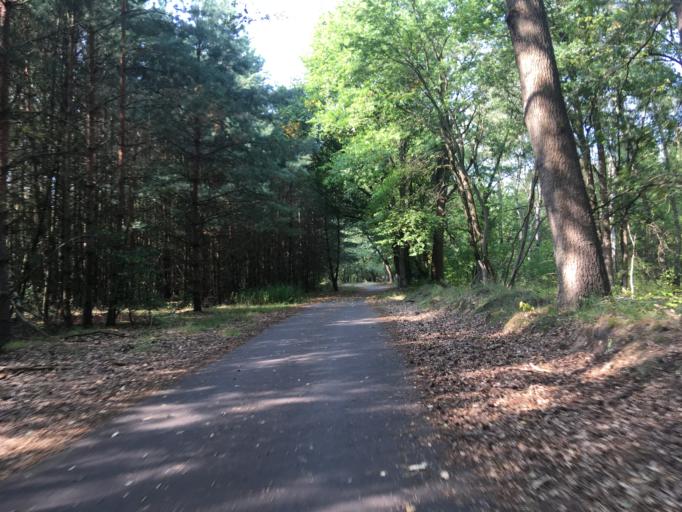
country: DE
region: Berlin
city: Falkenhagener Feld
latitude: 52.5965
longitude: 13.1712
